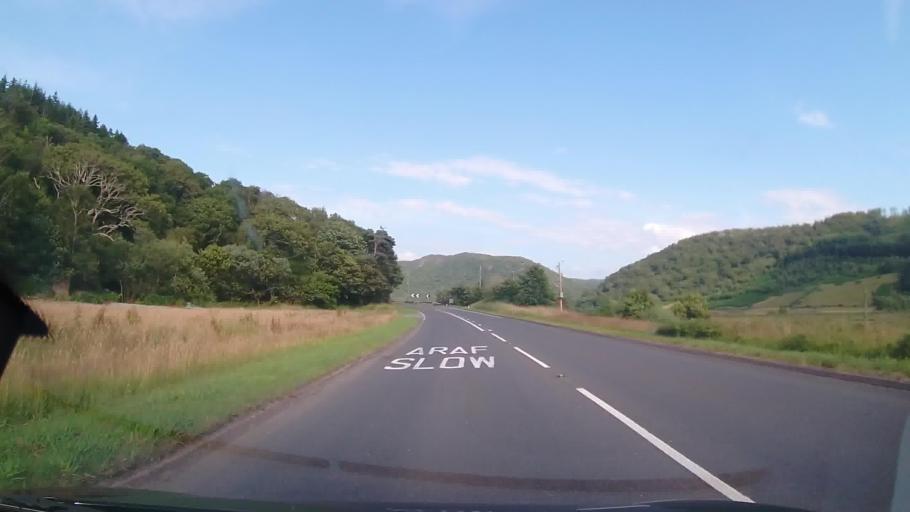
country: GB
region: Wales
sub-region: Gwynedd
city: Maentwrog
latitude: 52.9397
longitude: -4.0233
